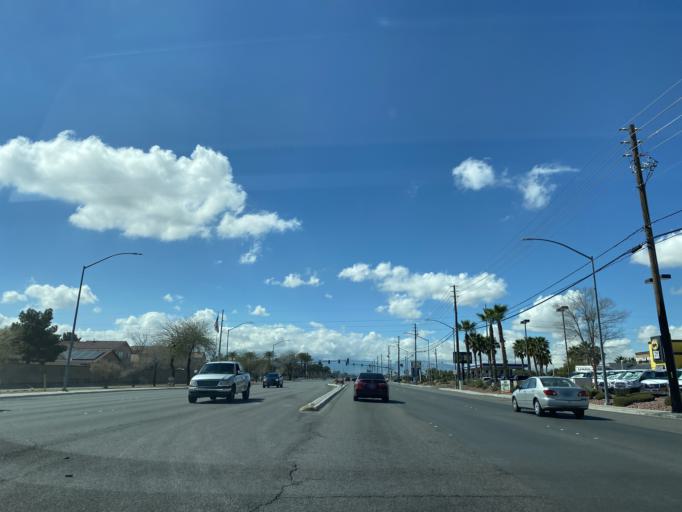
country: US
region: Nevada
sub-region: Clark County
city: North Las Vegas
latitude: 36.2396
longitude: -115.1412
